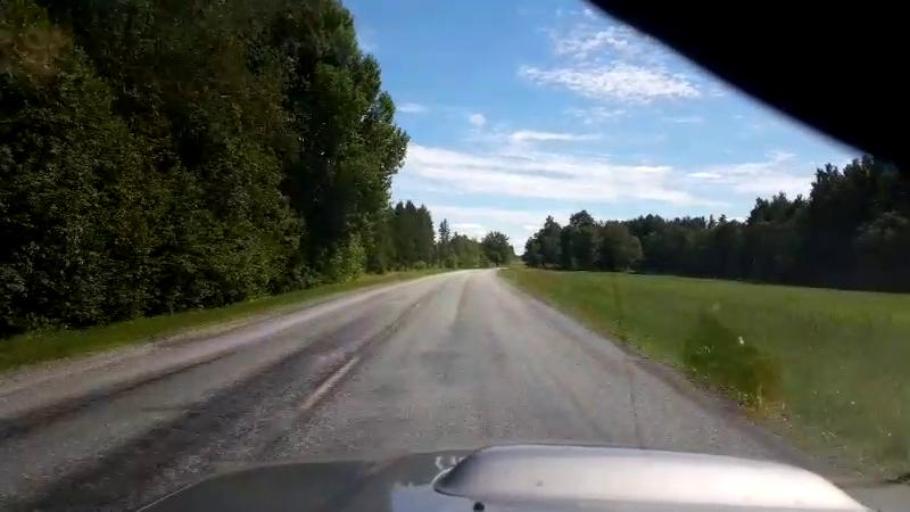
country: EE
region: Laeaene-Virumaa
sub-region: Rakke vald
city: Rakke
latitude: 58.8825
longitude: 26.2931
